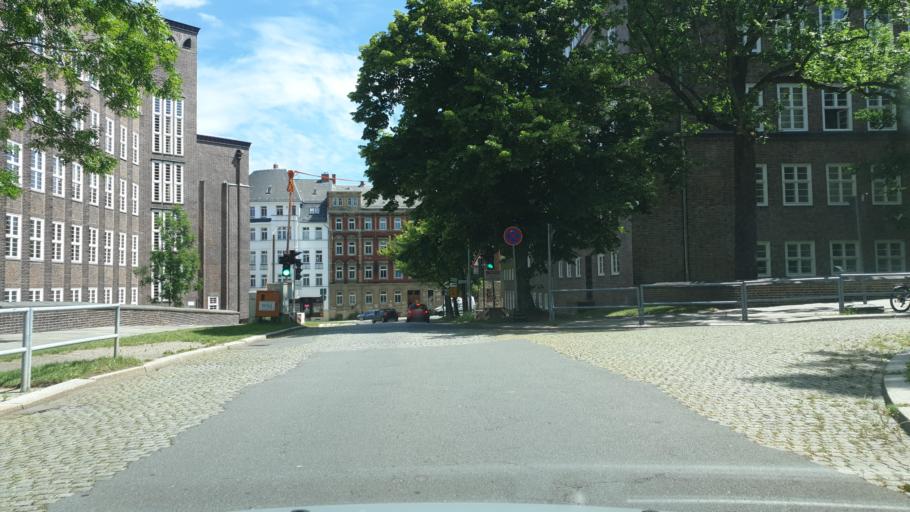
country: DE
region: Saxony
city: Chemnitz
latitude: 50.8306
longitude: 12.9297
